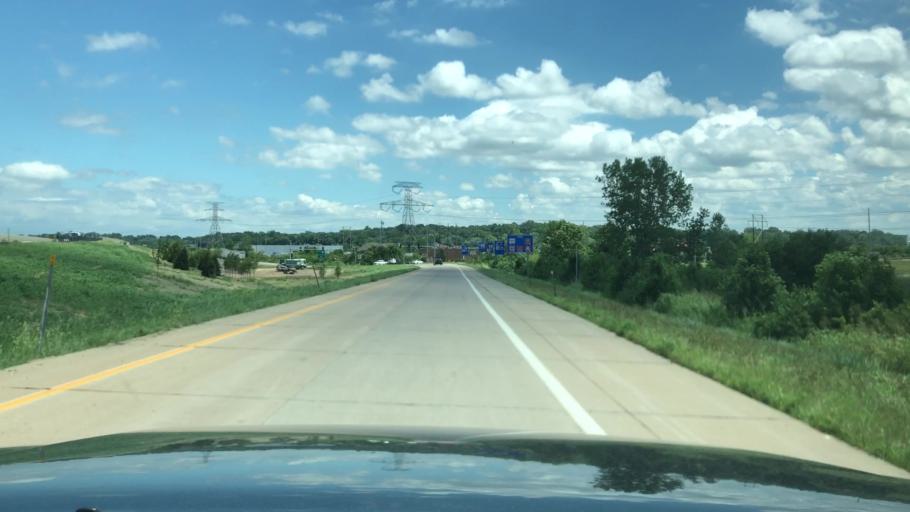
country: US
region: Missouri
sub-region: Saint Charles County
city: Saint Charles
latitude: 38.8246
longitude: -90.5204
